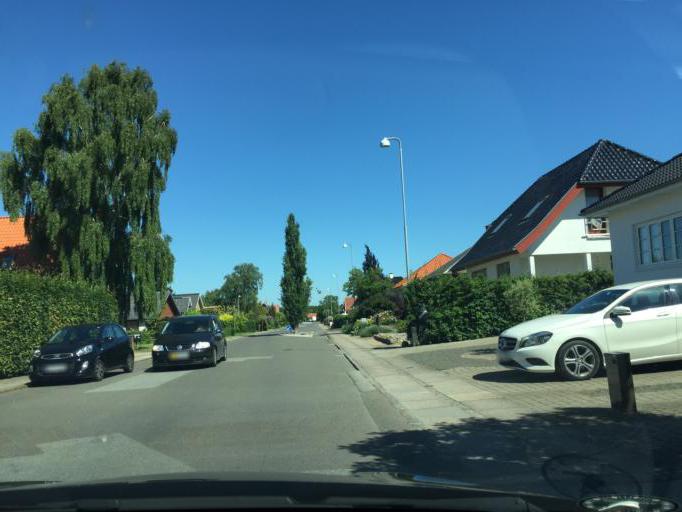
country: DK
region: South Denmark
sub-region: Odense Kommune
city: Odense
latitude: 55.3761
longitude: 10.3574
